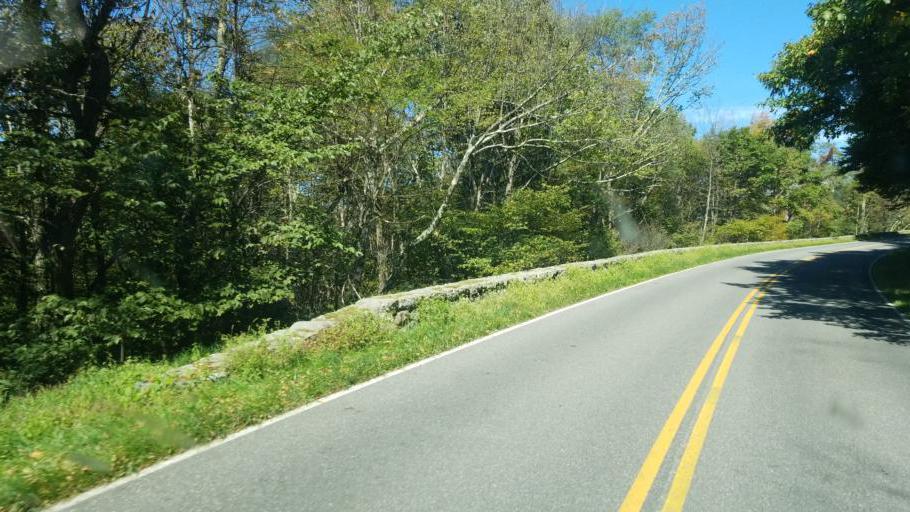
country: US
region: Virginia
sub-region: Rockingham County
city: Elkton
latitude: 38.3949
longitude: -78.5080
